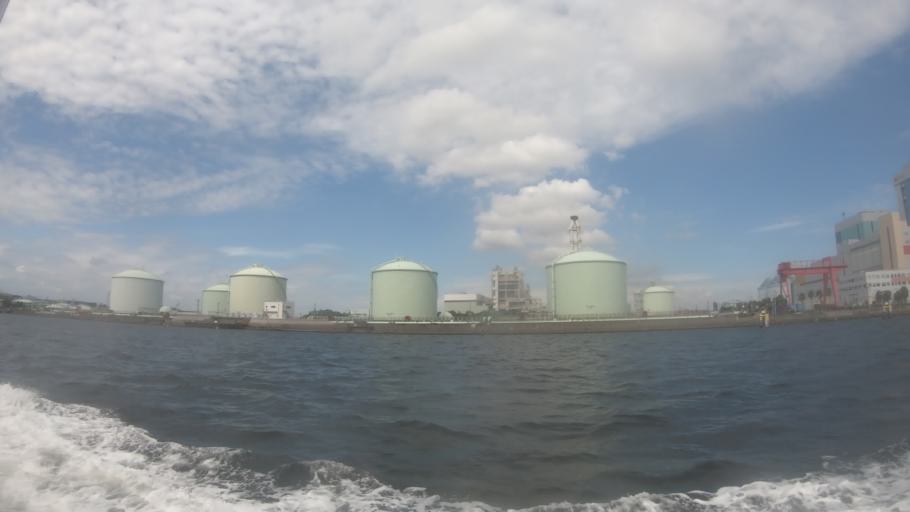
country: JP
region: Kanagawa
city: Yokohama
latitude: 35.4000
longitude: 139.6398
